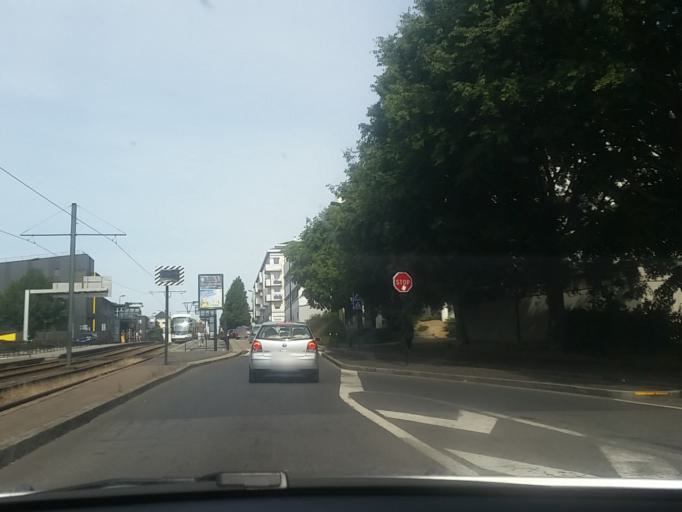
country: FR
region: Pays de la Loire
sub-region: Departement de la Loire-Atlantique
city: Nantes
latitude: 47.2074
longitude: -1.5806
